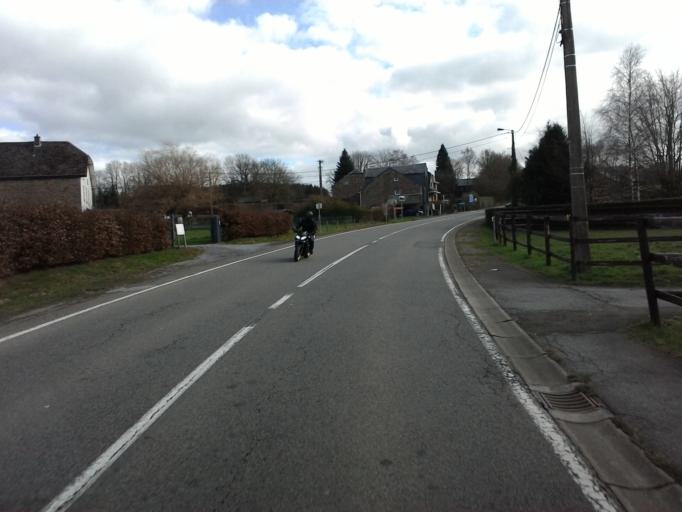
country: BE
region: Wallonia
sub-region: Province de Liege
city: Ferrieres
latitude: 50.3889
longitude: 5.6623
